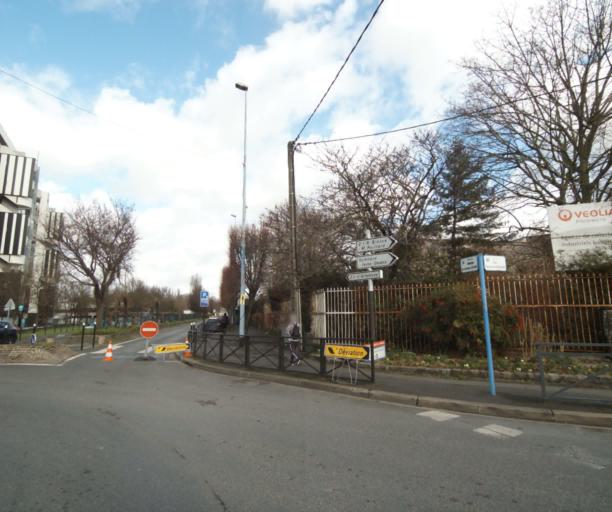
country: FR
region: Ile-de-France
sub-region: Departement de Seine-Saint-Denis
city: Villetaneuse
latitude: 48.9564
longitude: 2.3446
